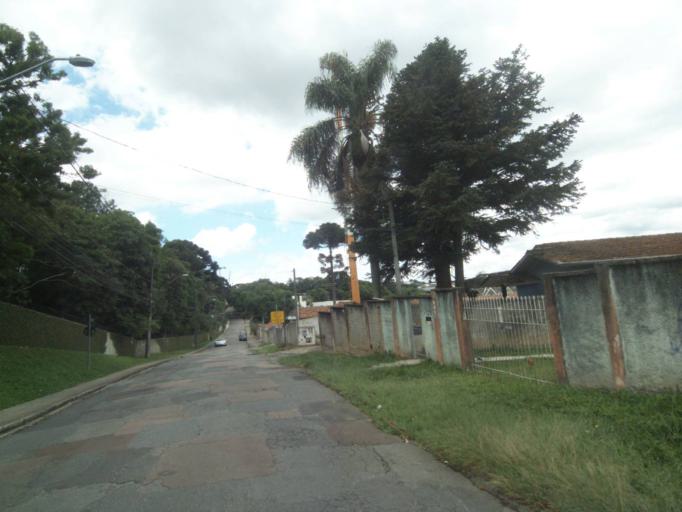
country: BR
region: Parana
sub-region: Curitiba
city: Curitiba
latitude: -25.4363
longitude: -49.3406
